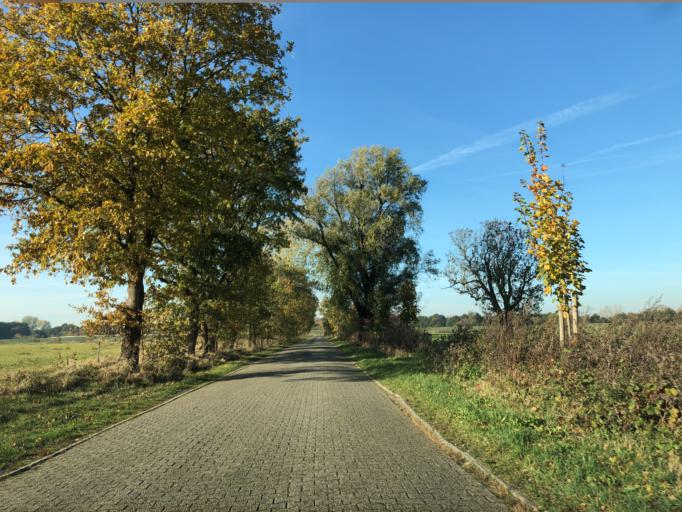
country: DE
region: Lower Saxony
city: Heede
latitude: 53.0330
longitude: 7.3068
